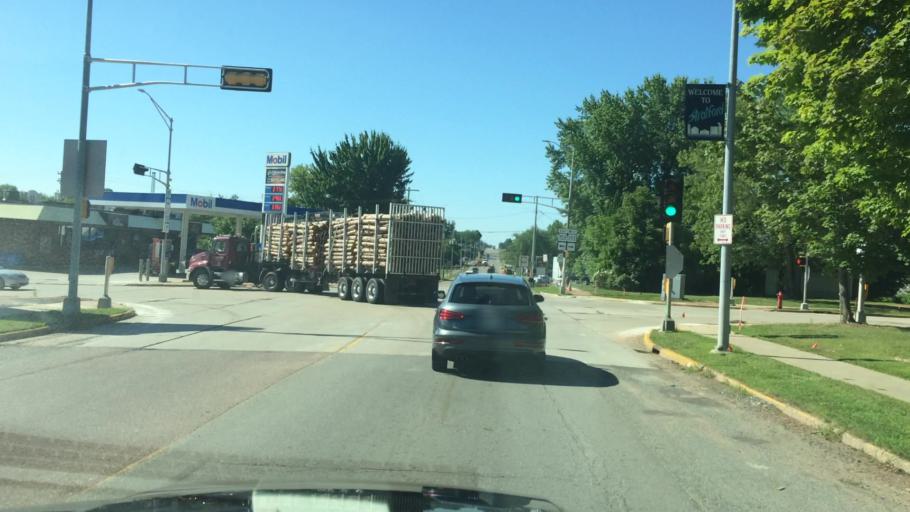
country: US
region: Wisconsin
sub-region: Marathon County
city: Stratford
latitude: 44.8012
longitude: -90.0792
